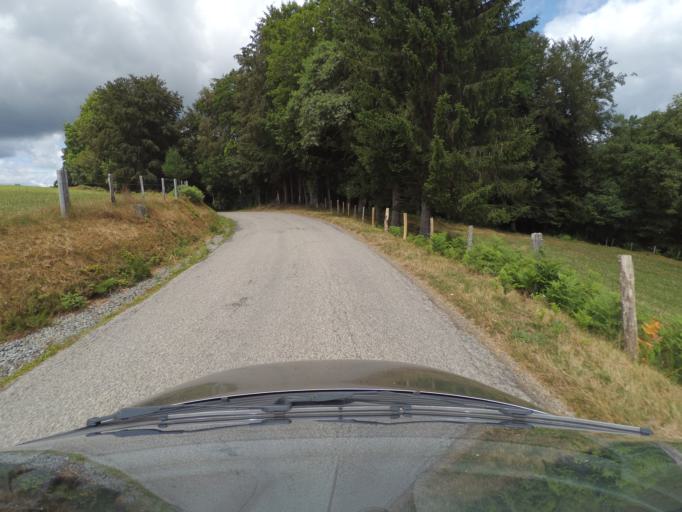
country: FR
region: Limousin
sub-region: Departement de la Creuse
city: Banize
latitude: 45.8163
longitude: 1.9303
